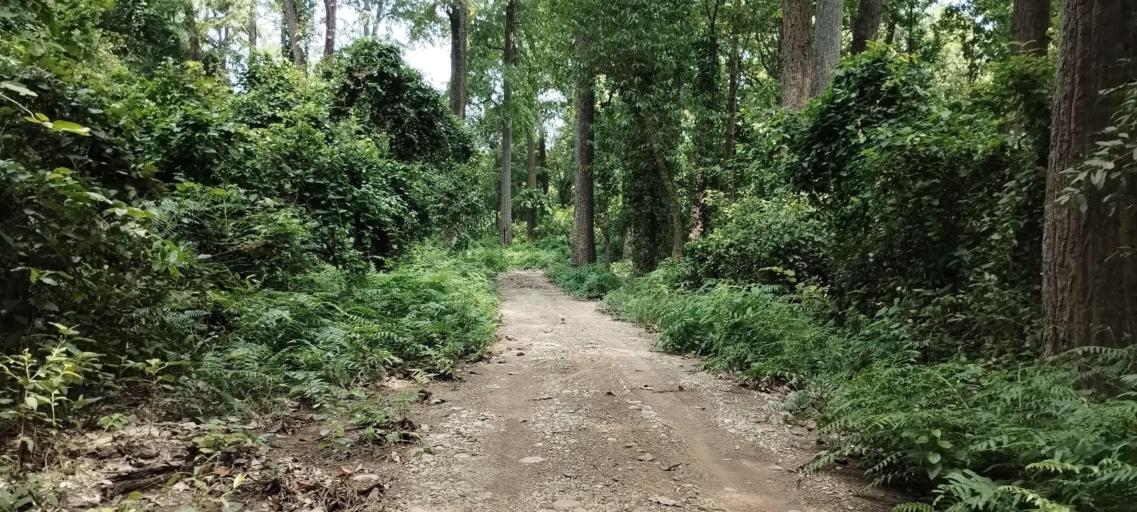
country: NP
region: Far Western
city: Tikapur
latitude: 28.4846
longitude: 81.2513
